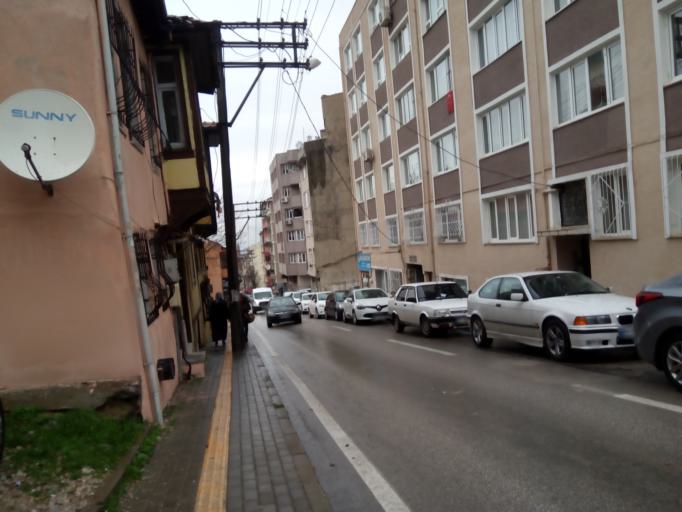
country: TR
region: Bursa
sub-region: Osmangazi
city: Bursa
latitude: 40.1790
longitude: 29.0619
